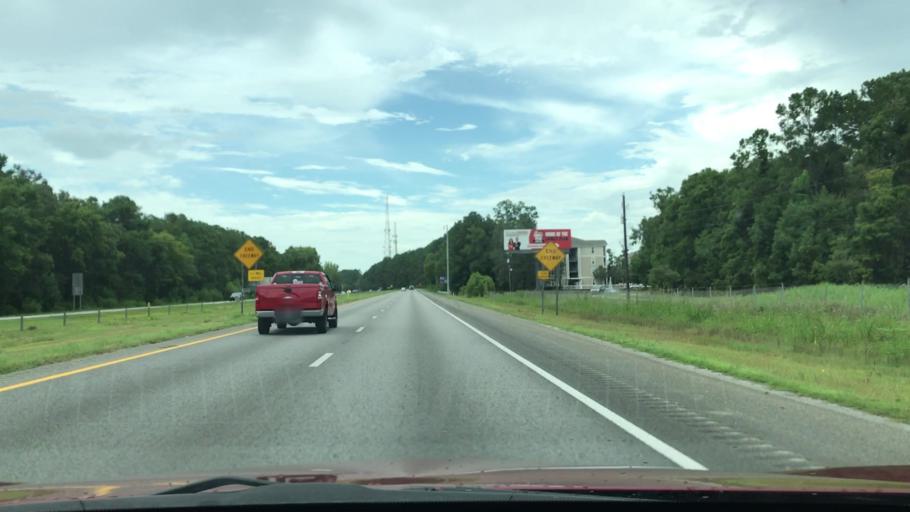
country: US
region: South Carolina
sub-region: Charleston County
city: Shell Point
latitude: 32.8015
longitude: -80.0361
